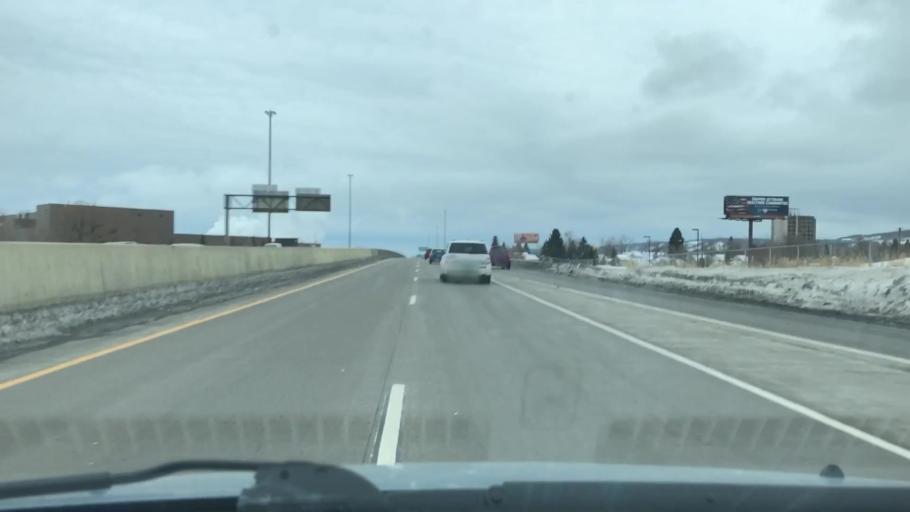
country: US
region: Wisconsin
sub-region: Douglas County
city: Superior
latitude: 46.7415
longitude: -92.1567
